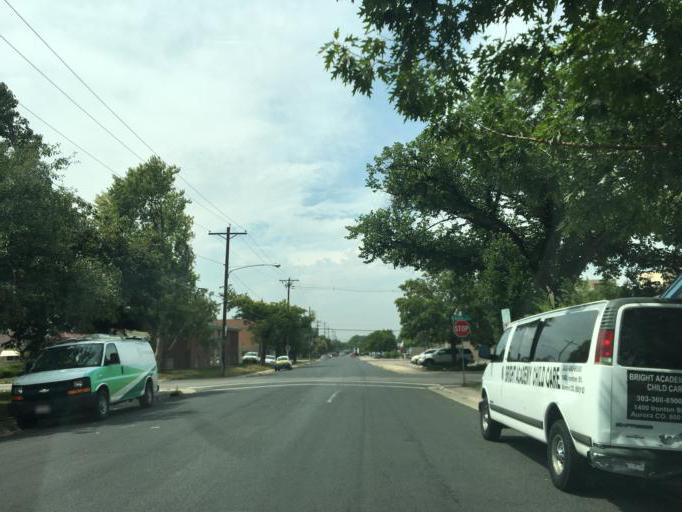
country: US
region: Colorado
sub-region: Adams County
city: Aurora
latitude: 39.7383
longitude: -104.8629
